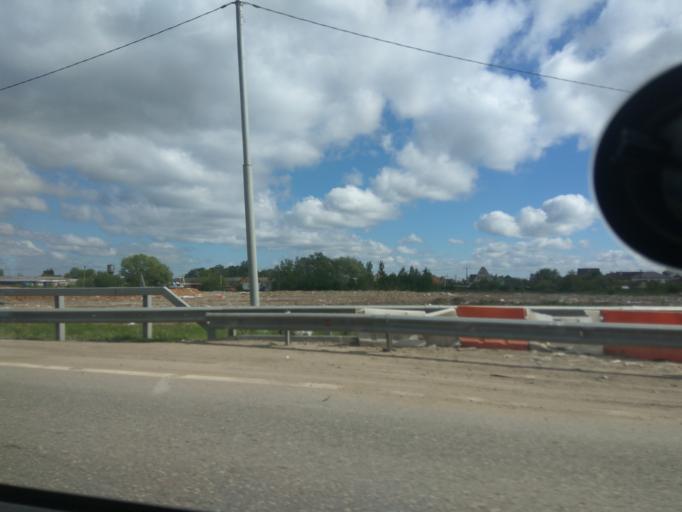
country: RU
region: Moskovskaya
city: Ostrovtsy
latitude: 55.5630
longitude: 38.0500
